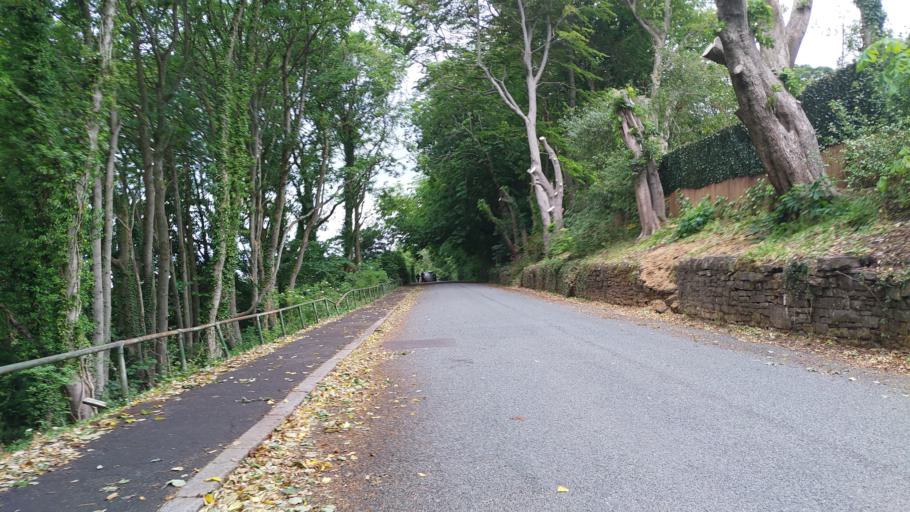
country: GB
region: England
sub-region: Lancashire
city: Chorley
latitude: 53.6901
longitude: -2.6047
